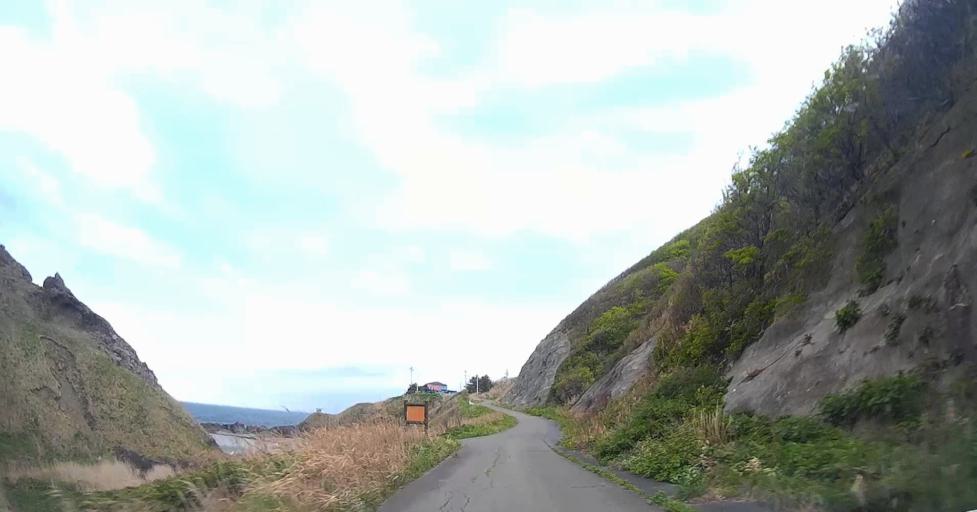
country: JP
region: Aomori
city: Shimokizukuri
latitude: 41.2415
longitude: 140.3428
